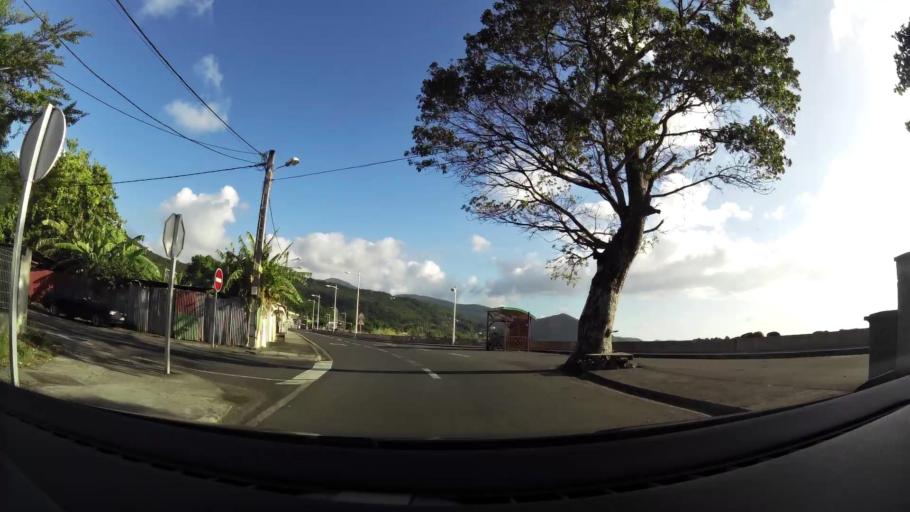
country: GP
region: Guadeloupe
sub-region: Guadeloupe
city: Pointe-Noire
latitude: 16.2298
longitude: -61.7883
